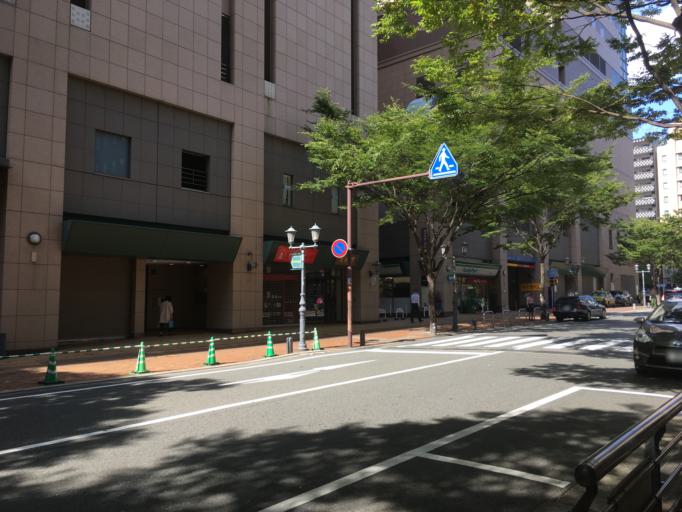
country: JP
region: Fukuoka
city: Fukuoka-shi
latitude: 33.5954
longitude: 130.4058
